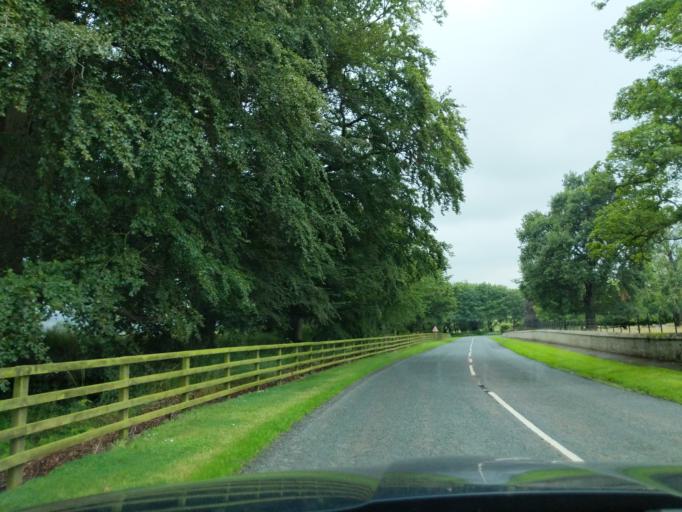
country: GB
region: England
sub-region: Northumberland
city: Ford
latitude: 55.6286
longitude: -2.0911
